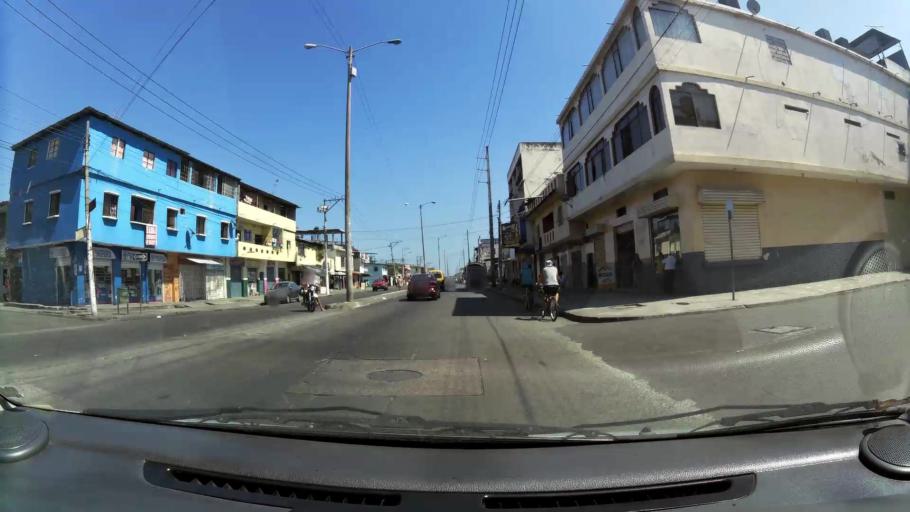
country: EC
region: Guayas
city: Guayaquil
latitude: -2.2221
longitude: -79.9409
